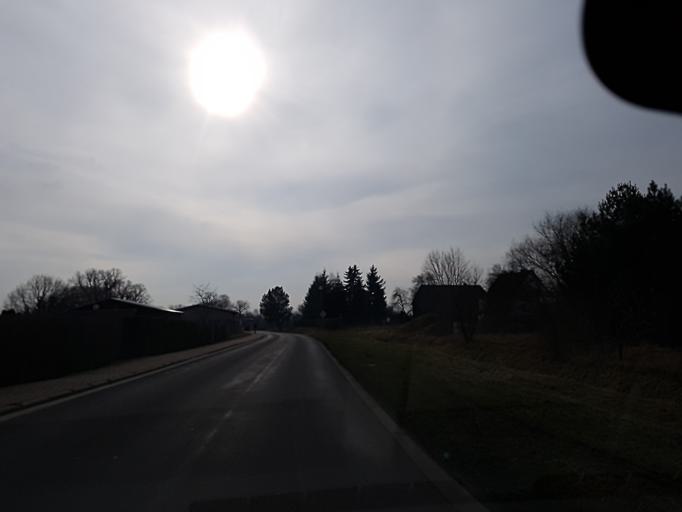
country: DE
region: Brandenburg
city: Doberlug-Kirchhain
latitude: 51.6244
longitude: 13.5571
